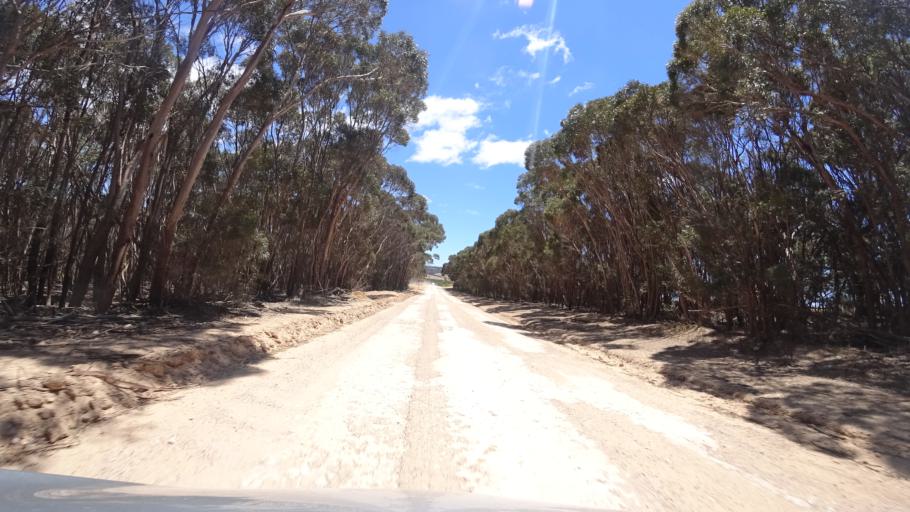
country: AU
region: South Australia
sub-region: Yankalilla
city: Normanville
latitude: -35.8126
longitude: 138.0734
